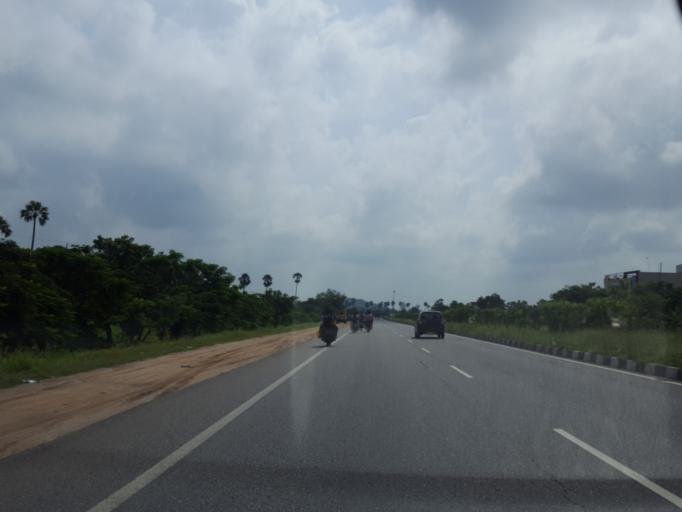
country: IN
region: Telangana
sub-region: Nalgonda
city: Bhongir
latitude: 17.2301
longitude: 78.9699
